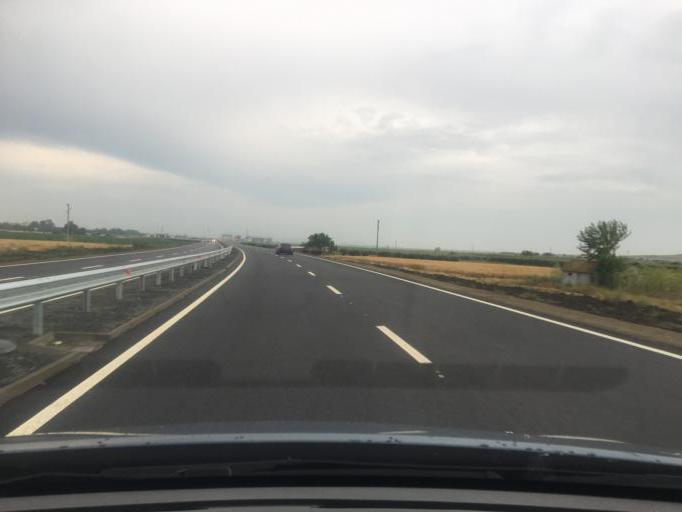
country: BG
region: Burgas
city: Aheloy
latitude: 42.6510
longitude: 27.6371
